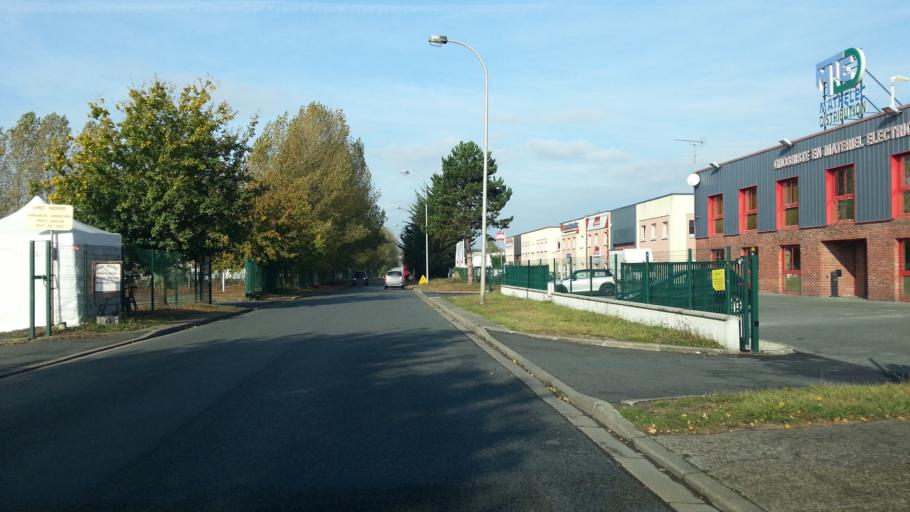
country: FR
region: Picardie
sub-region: Departement de l'Oise
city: Saint-Maximin
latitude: 49.2393
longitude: 2.4615
